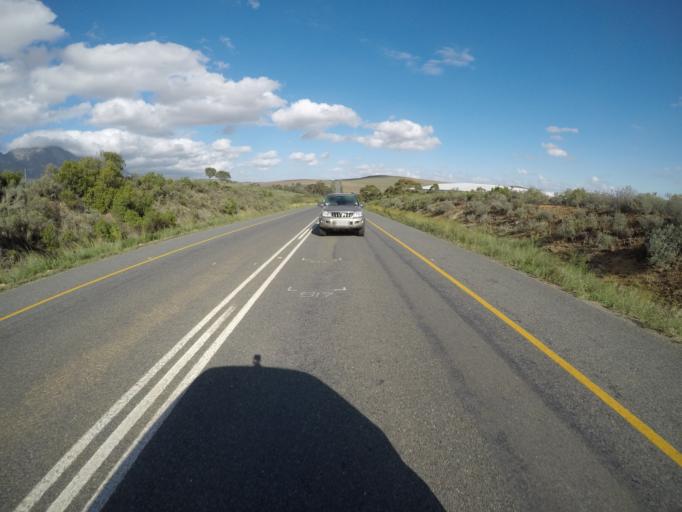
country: ZA
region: Western Cape
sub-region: Overberg District Municipality
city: Swellendam
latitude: -33.9590
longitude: 20.2386
